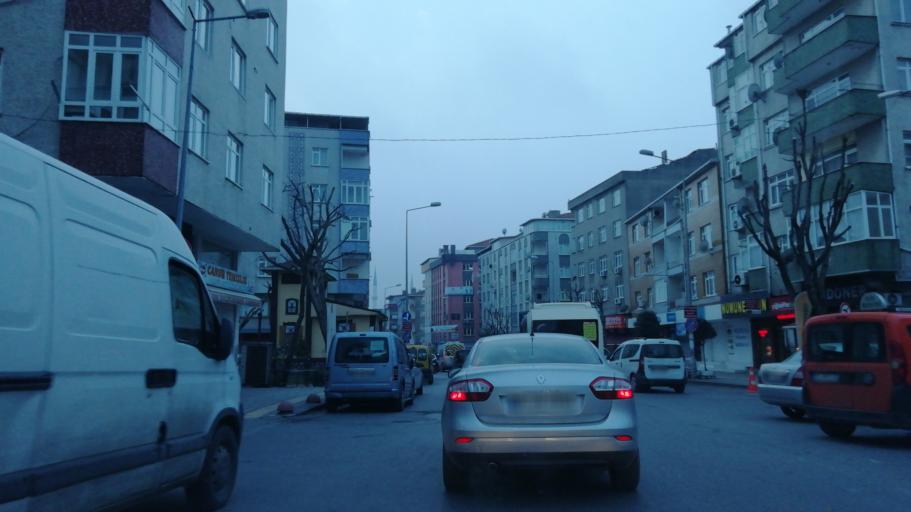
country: TR
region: Istanbul
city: Bahcelievler
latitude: 41.0022
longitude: 28.8303
